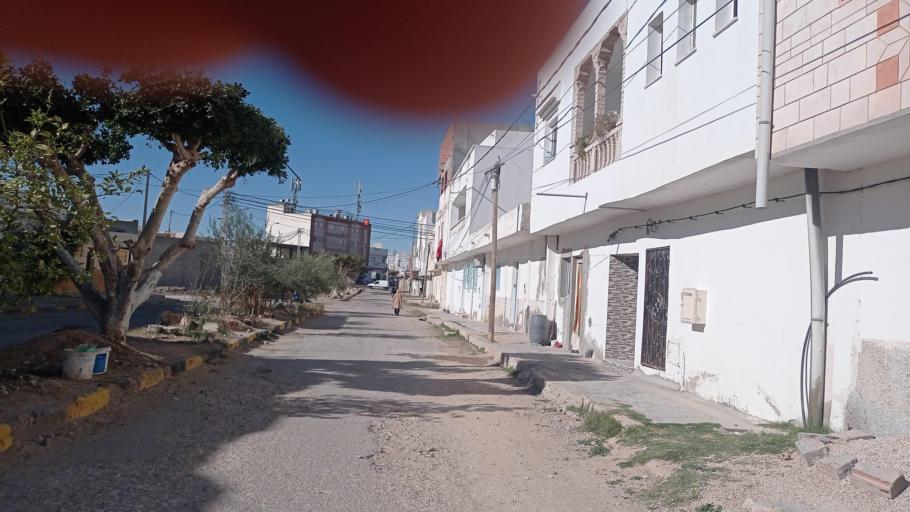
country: TN
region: Qabis
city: Gabes
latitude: 33.8439
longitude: 10.1146
